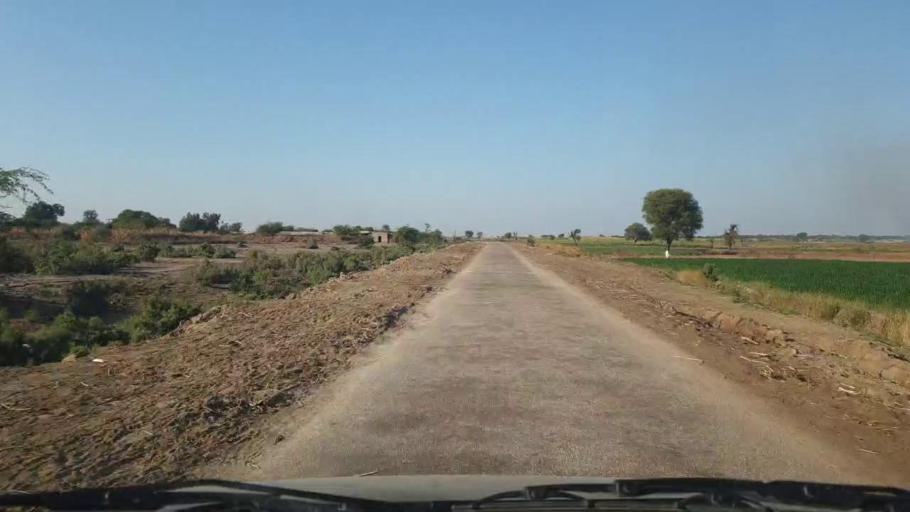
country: PK
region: Sindh
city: Samaro
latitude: 25.3450
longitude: 69.2995
